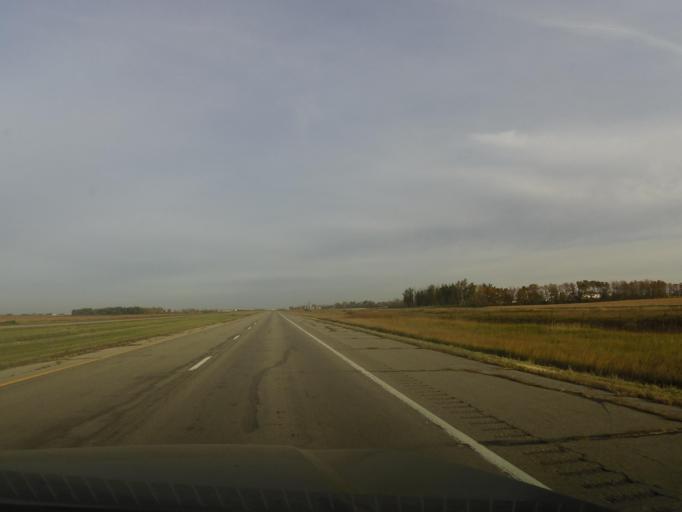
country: US
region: Minnesota
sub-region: Kittson County
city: Hallock
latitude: 48.7475
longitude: -97.2000
